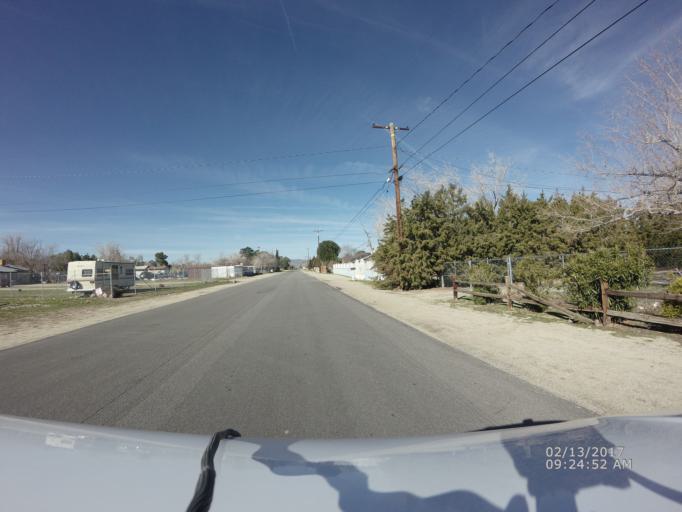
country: US
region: California
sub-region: Los Angeles County
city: Littlerock
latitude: 34.5303
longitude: -117.9611
